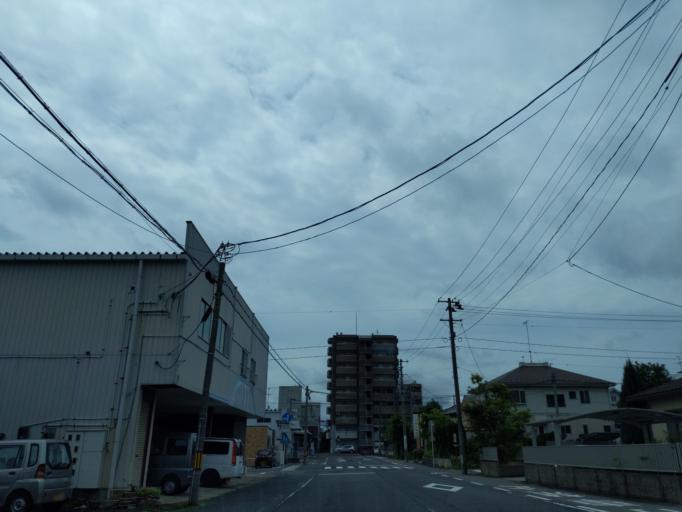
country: JP
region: Fukushima
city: Koriyama
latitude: 37.3922
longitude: 140.3545
